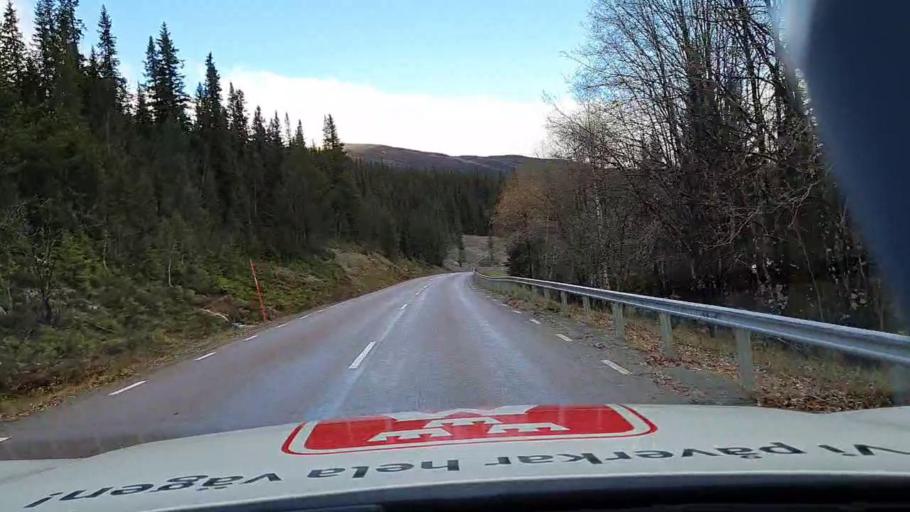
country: SE
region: Jaemtland
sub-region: Are Kommun
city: Jarpen
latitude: 63.0900
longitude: 13.7722
